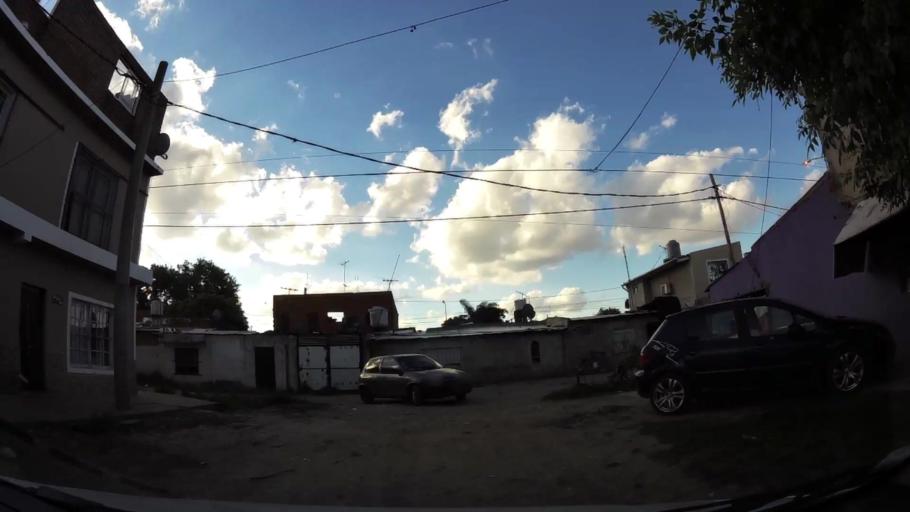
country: AR
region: Buenos Aires
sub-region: Partido de Moron
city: Moron
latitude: -34.7081
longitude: -58.6179
